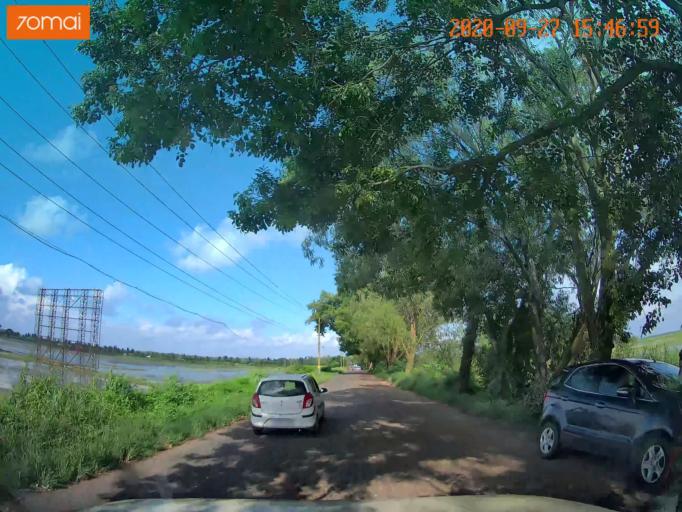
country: IN
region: Kerala
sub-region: Thrissur District
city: Thanniyam
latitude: 10.4812
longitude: 76.1257
